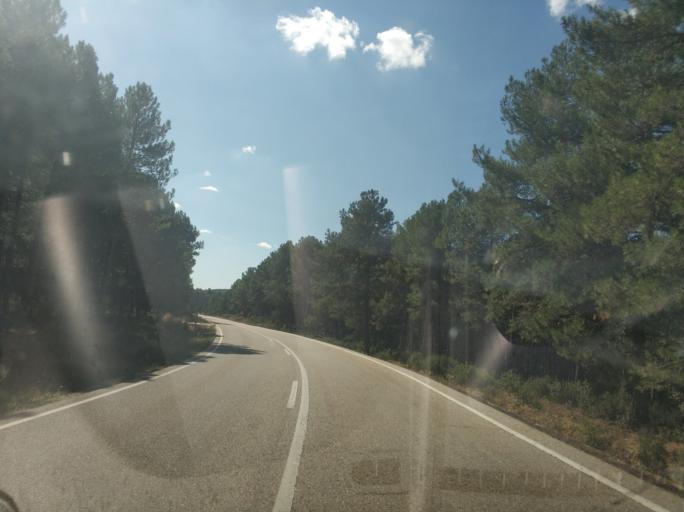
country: ES
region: Castille and Leon
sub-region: Provincia de Soria
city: Ucero
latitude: 41.7458
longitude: -3.0437
